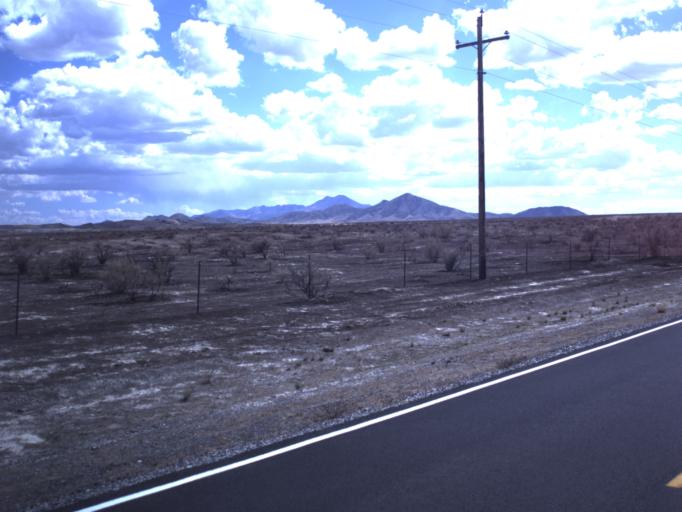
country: US
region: Utah
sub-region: Tooele County
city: Grantsville
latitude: 40.2414
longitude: -112.7132
